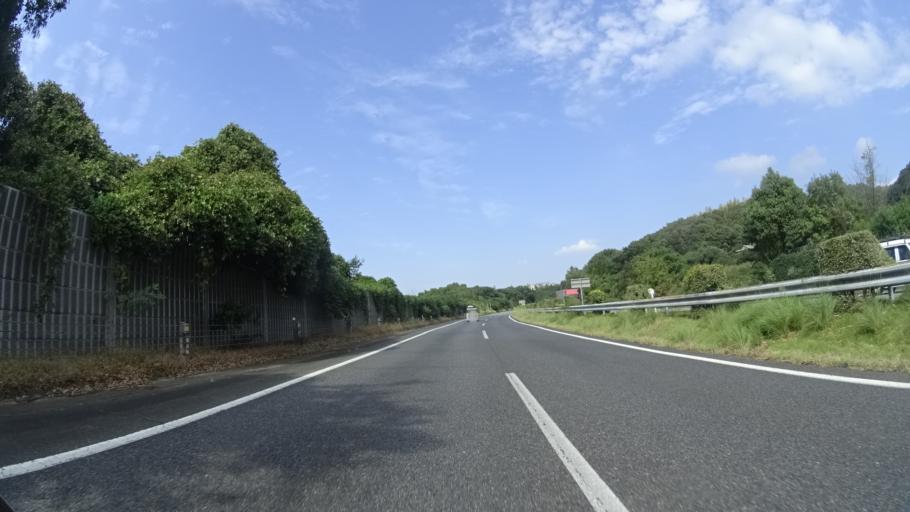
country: JP
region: Kumamoto
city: Matsubase
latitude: 32.6205
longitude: 130.7140
